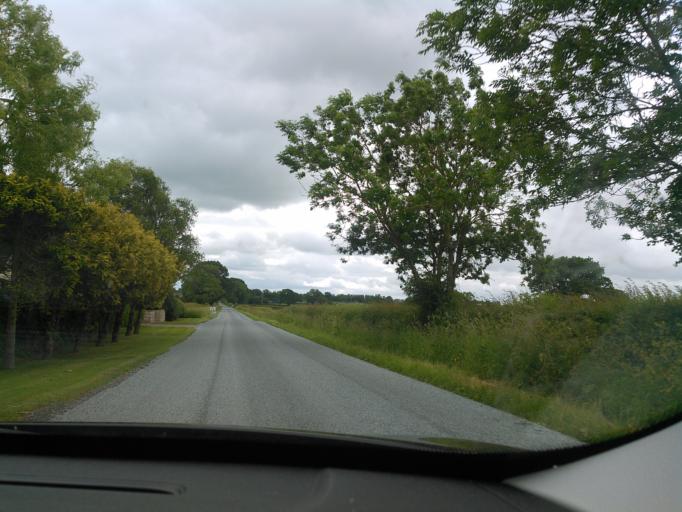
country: GB
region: England
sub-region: Shropshire
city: Wem
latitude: 52.8975
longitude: -2.7618
